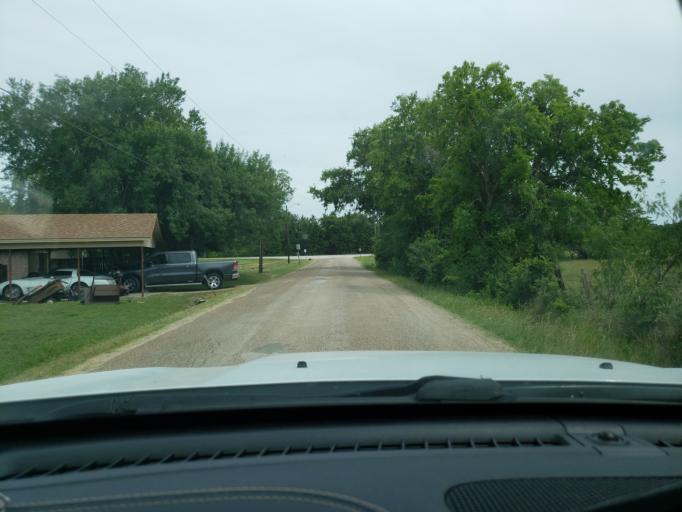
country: US
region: Texas
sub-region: Burleson County
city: Somerville
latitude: 30.3496
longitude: -96.5413
